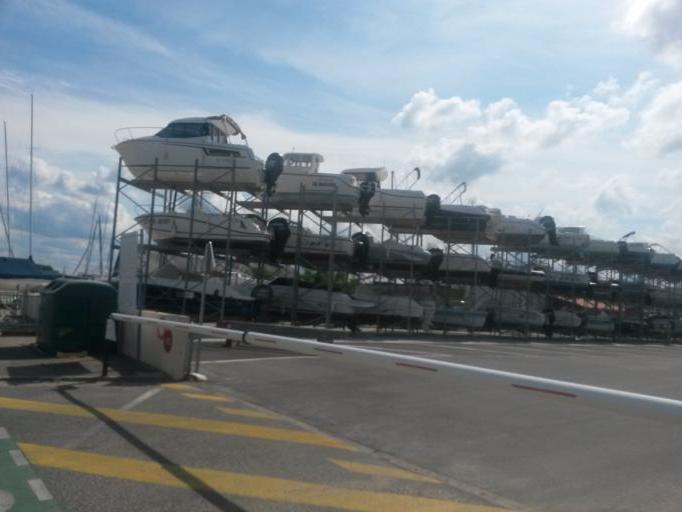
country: FR
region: Aquitaine
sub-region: Departement de la Gironde
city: Arcachon
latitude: 44.6598
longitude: -1.1435
